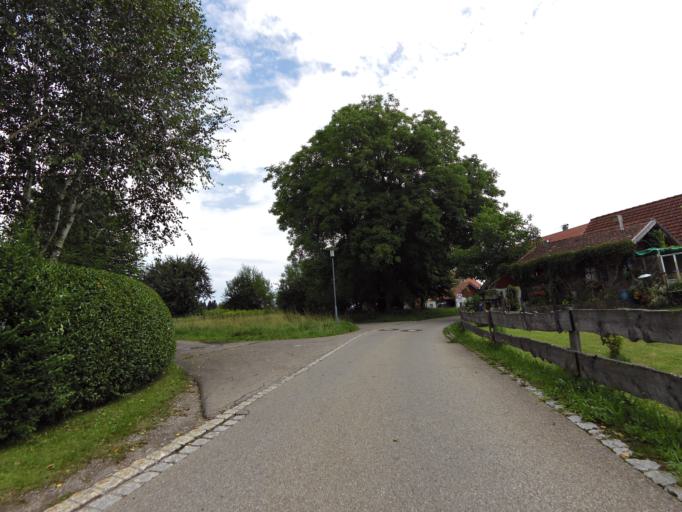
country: DE
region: Bavaria
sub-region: Swabia
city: Heimenkirch
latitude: 47.6087
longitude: 9.9196
